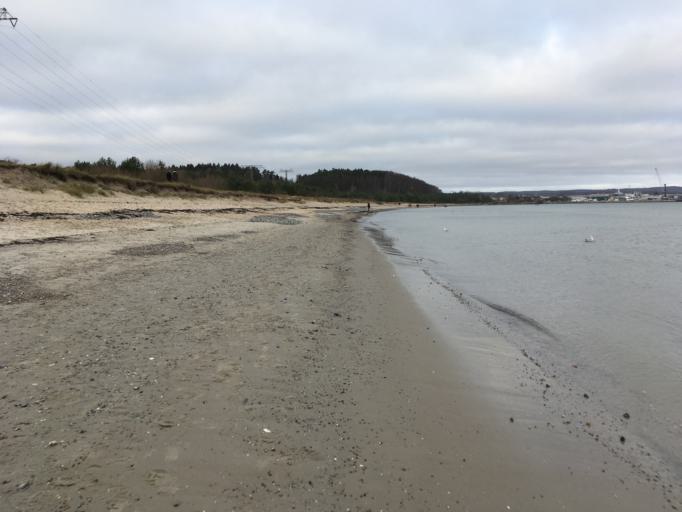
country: DE
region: Mecklenburg-Vorpommern
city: Sagard
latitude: 54.4720
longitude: 13.5710
